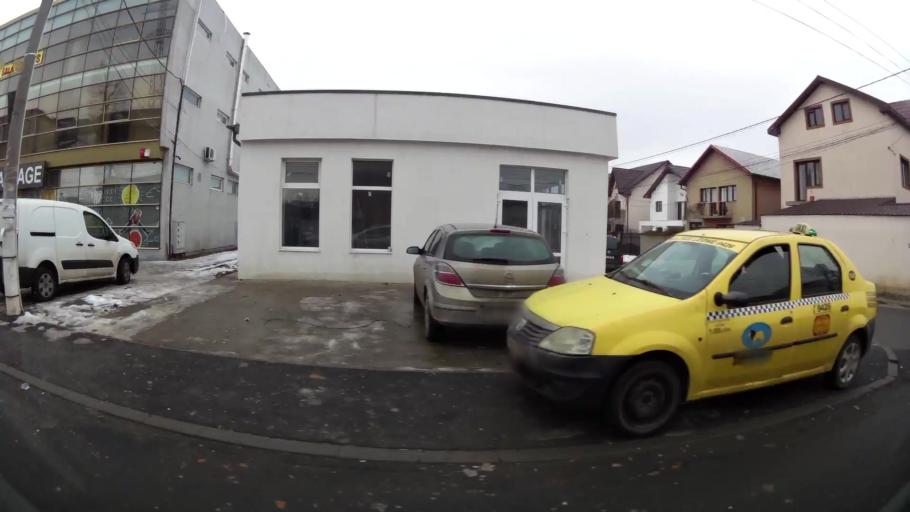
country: RO
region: Ilfov
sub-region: Comuna Pantelimon
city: Pantelimon
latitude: 44.4620
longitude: 26.2113
